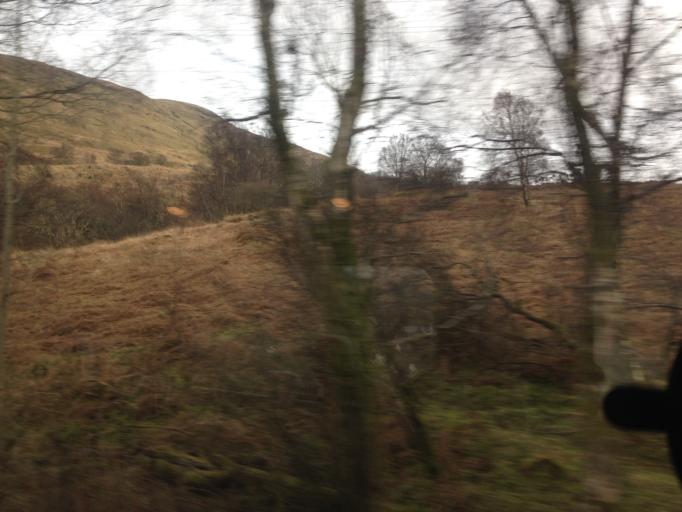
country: GB
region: Scotland
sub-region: Argyll and Bute
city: Garelochhead
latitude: 56.1908
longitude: -4.7500
